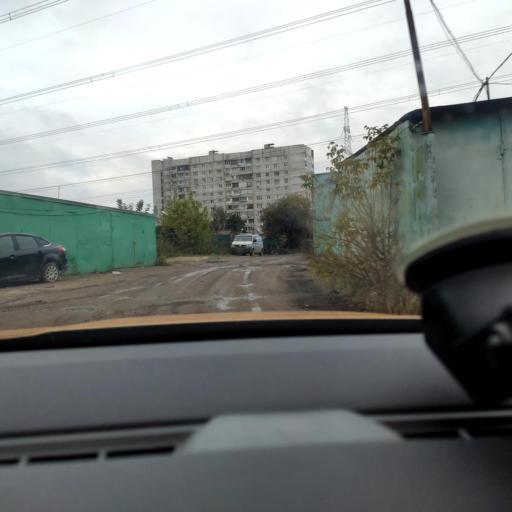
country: RU
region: Moscow
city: Bibirevo
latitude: 55.8827
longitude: 37.6115
